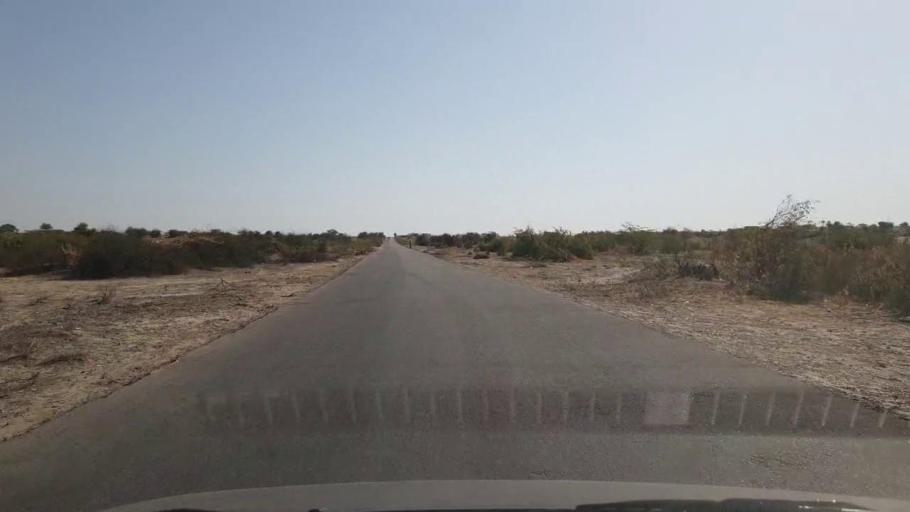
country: PK
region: Sindh
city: Chor
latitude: 25.4880
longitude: 69.7865
